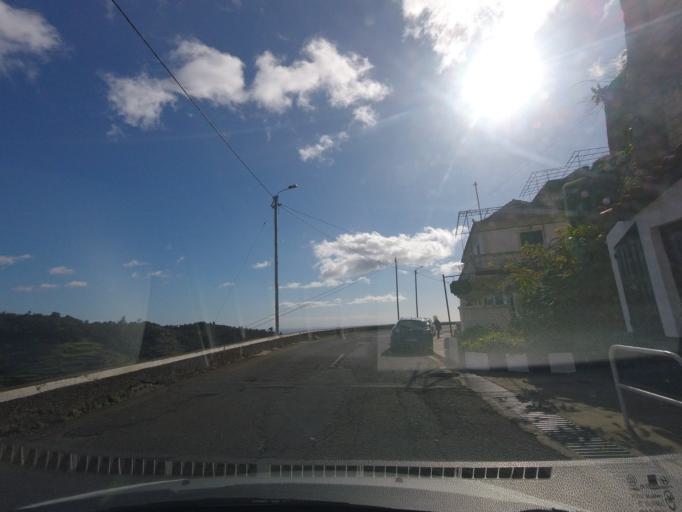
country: PT
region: Madeira
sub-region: Ribeira Brava
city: Campanario
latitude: 32.6613
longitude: -17.0141
